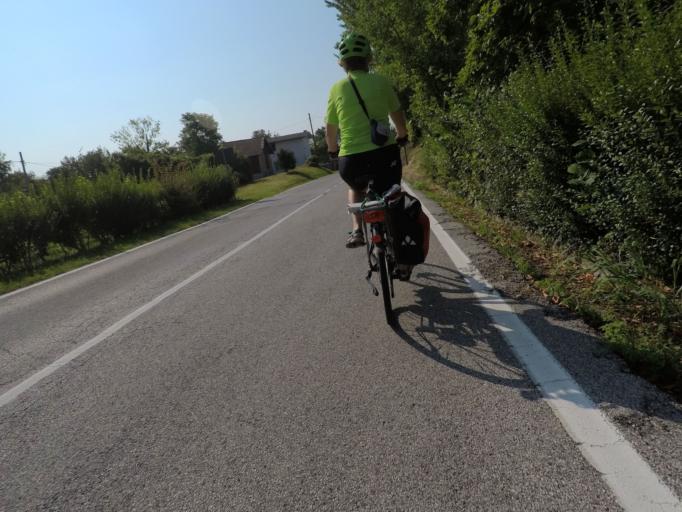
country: IT
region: Friuli Venezia Giulia
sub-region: Provincia di Pordenone
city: Pinzano al Tagliamento
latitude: 46.1837
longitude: 12.9504
